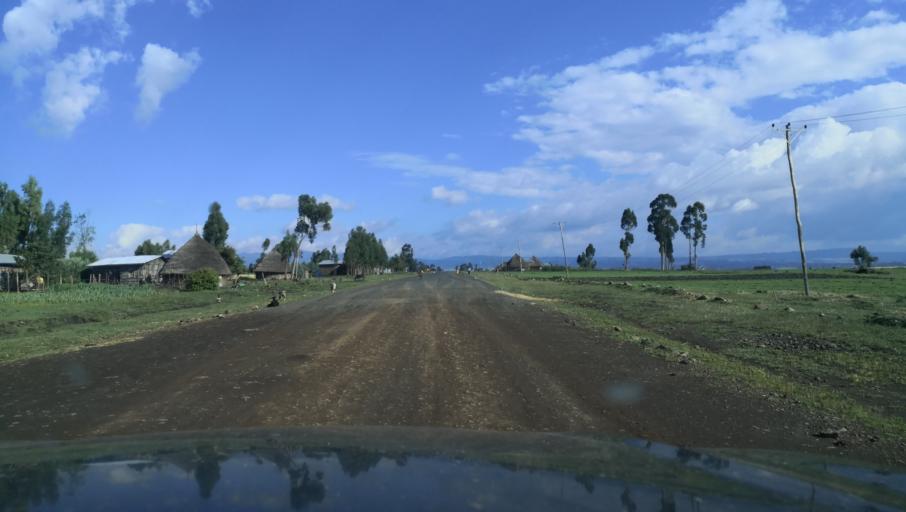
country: ET
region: Oromiya
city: Tulu Bolo
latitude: 8.5365
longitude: 38.2541
